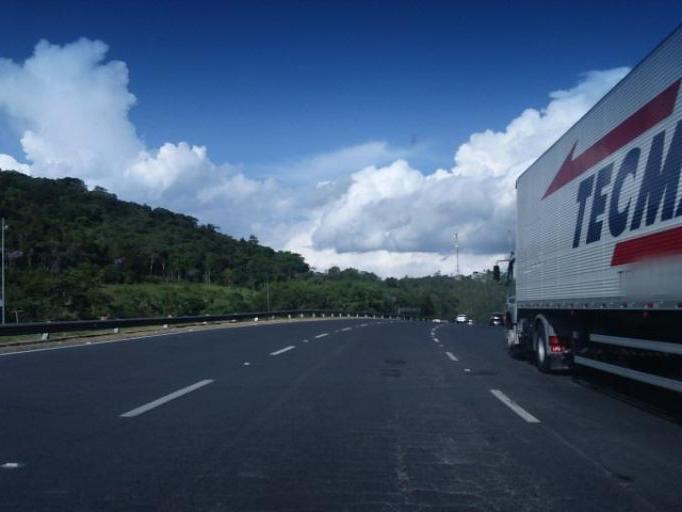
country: BR
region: Sao Paulo
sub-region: Juquia
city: Juquia
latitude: -24.3883
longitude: -47.7211
